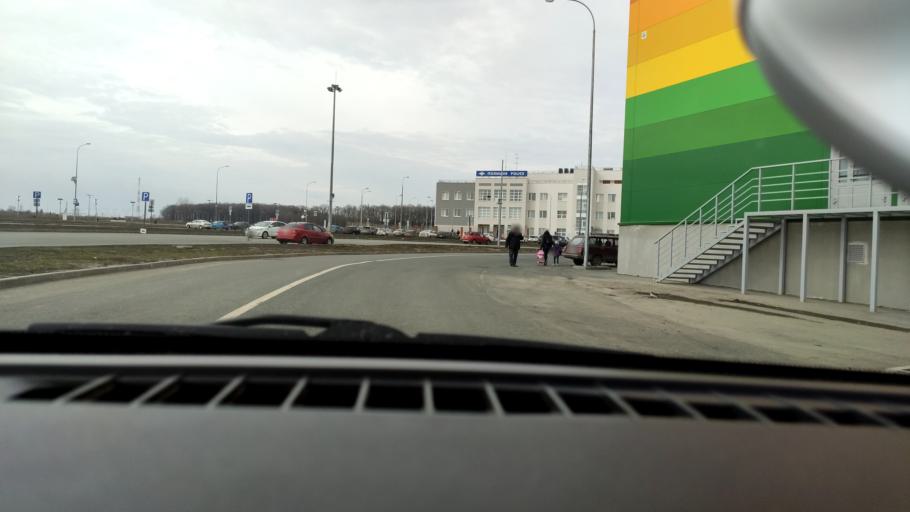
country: RU
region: Samara
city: Petra-Dubrava
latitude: 53.2753
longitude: 50.2545
